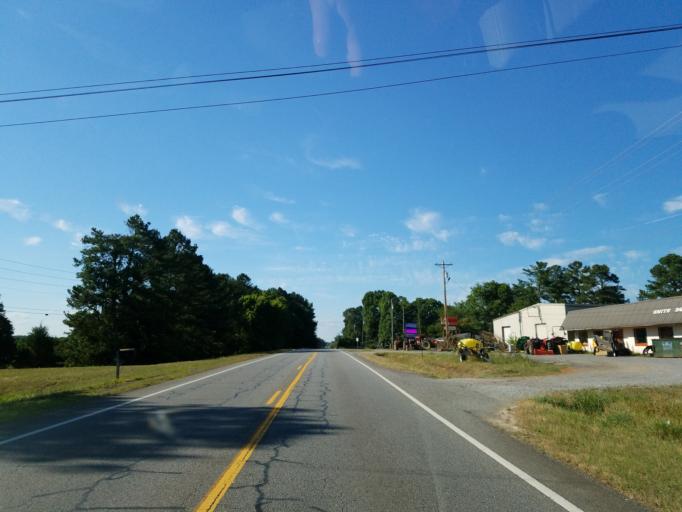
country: US
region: Georgia
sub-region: Bartow County
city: Adairsville
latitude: 34.4293
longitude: -84.9344
